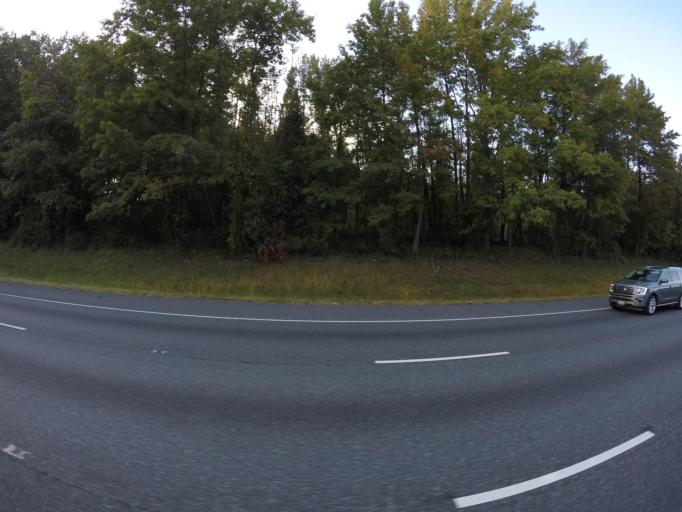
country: US
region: Maryland
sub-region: Harford County
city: Perryman
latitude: 39.5108
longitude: -76.2109
